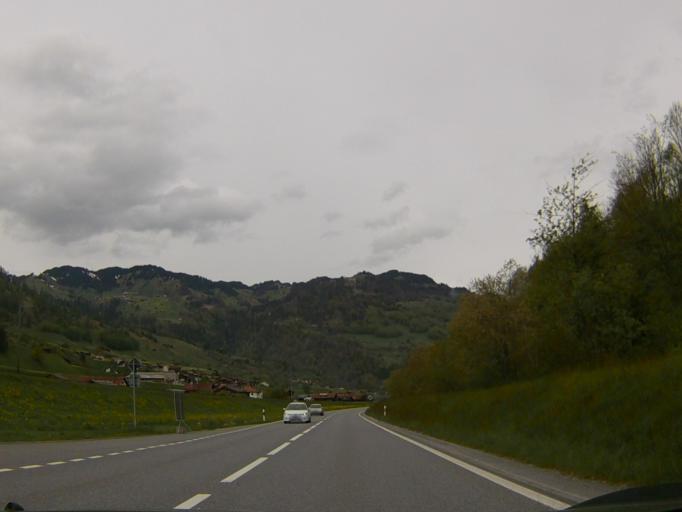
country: CH
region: Grisons
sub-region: Praettigau/Davos District
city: Jenaz
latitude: 46.9248
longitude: 9.7256
